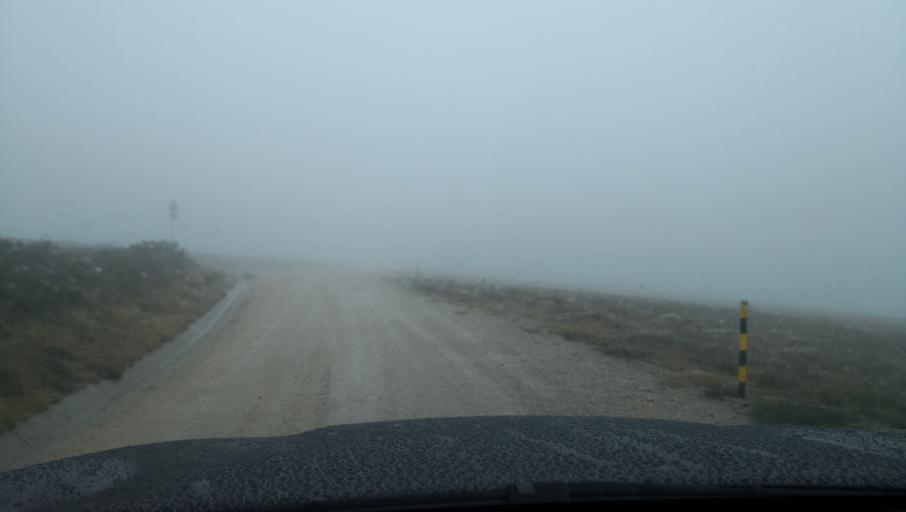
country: PT
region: Vila Real
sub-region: Vila Real
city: Vila Real
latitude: 41.3345
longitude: -7.8368
